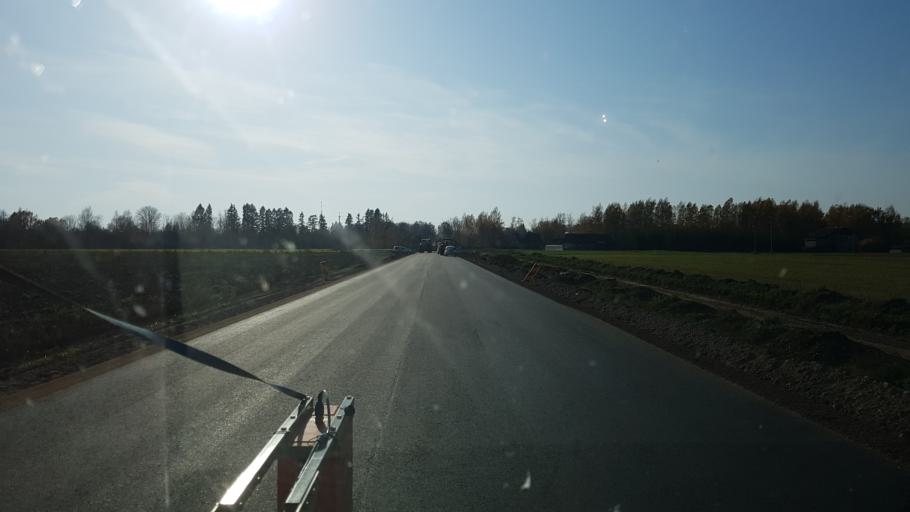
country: EE
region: Vorumaa
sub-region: Antsla vald
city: Vana-Antsla
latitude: 57.8367
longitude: 26.5442
